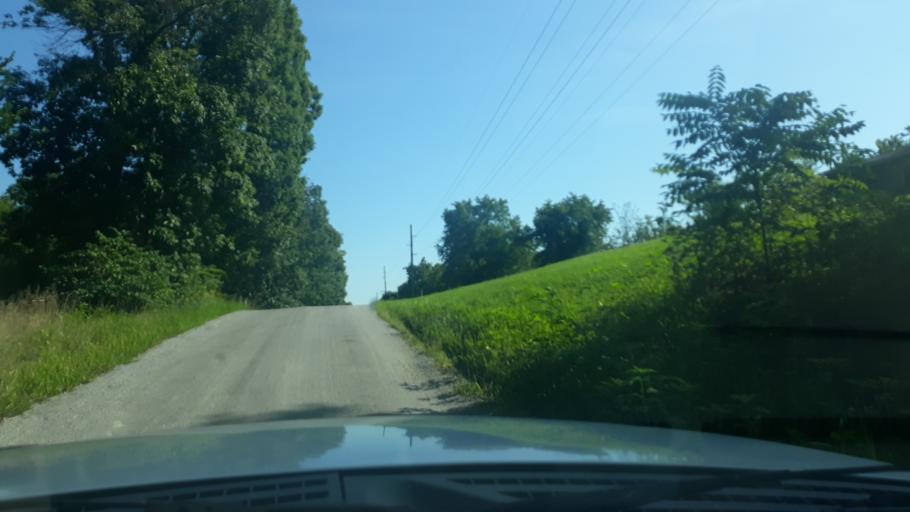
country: US
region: Illinois
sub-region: Saline County
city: Harrisburg
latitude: 37.8531
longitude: -88.5963
